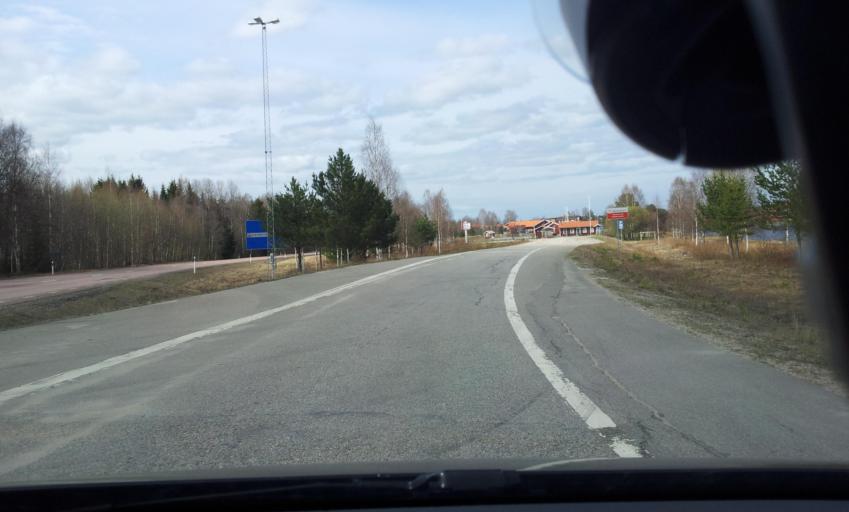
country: SE
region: Gaevleborg
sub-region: Ljusdals Kommun
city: Ljusdal
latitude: 61.8181
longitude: 16.0692
